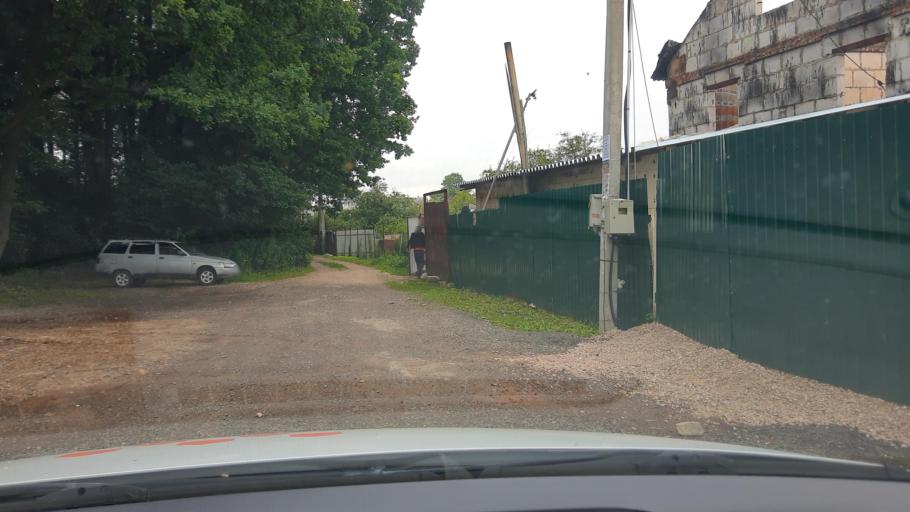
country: RU
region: Moskovskaya
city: Gorki-Leninskiye
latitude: 55.5002
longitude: 37.8308
